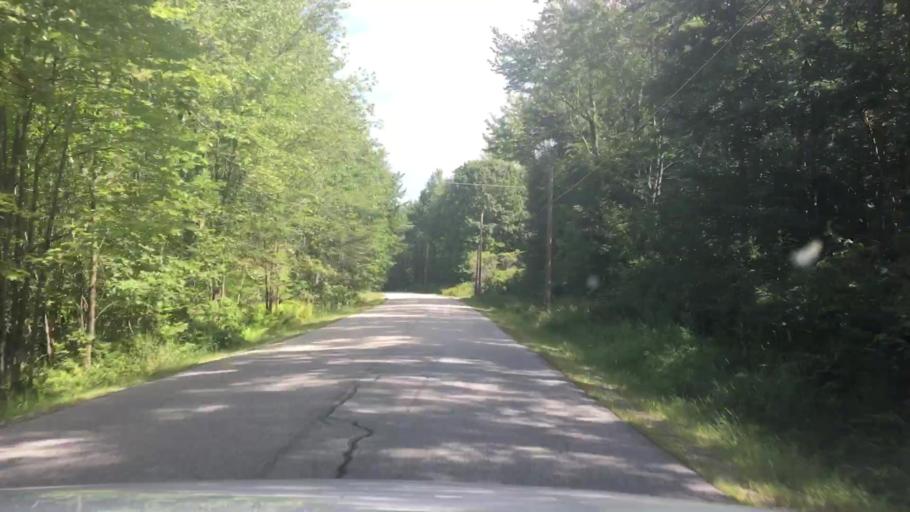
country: US
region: Maine
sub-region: Androscoggin County
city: Turner
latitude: 44.1856
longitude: -70.2622
